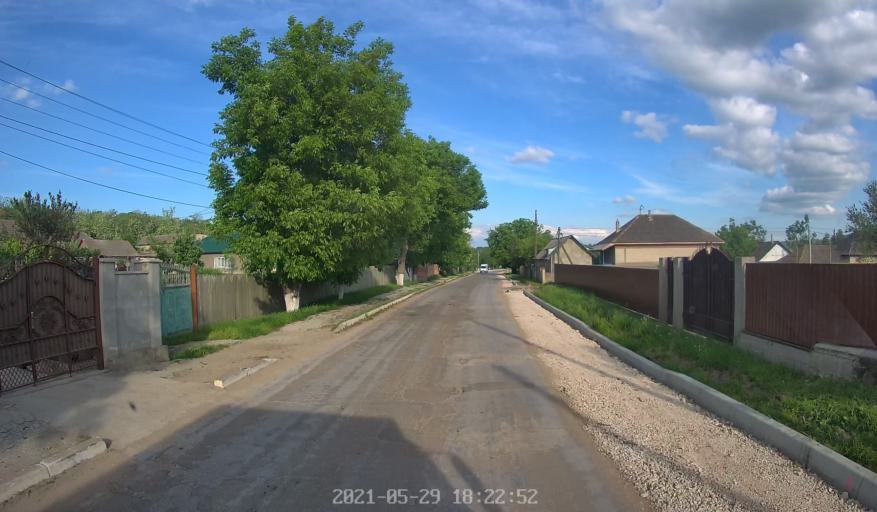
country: MD
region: Laloveni
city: Ialoveni
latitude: 46.8351
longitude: 28.8511
